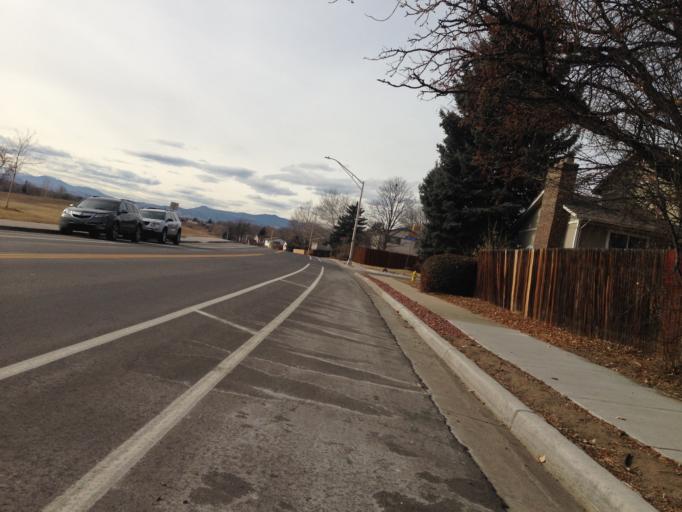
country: US
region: Colorado
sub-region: Adams County
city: Westminster
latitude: 39.8459
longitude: -105.0682
